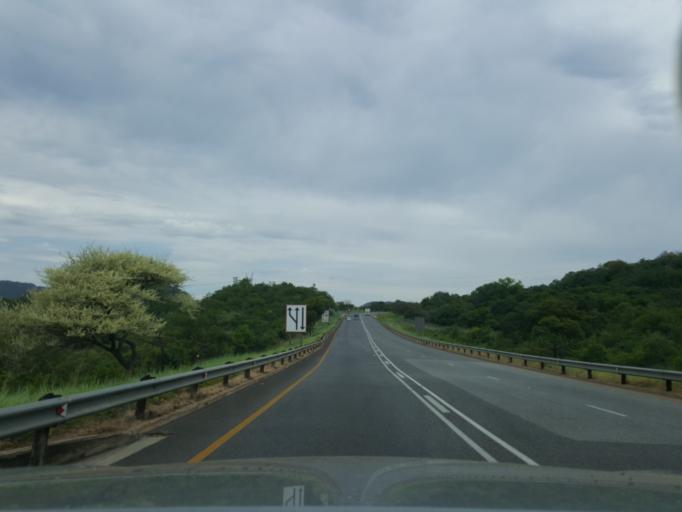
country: ZA
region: Mpumalanga
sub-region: Ehlanzeni District
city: Nelspruit
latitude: -25.4886
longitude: 31.1212
